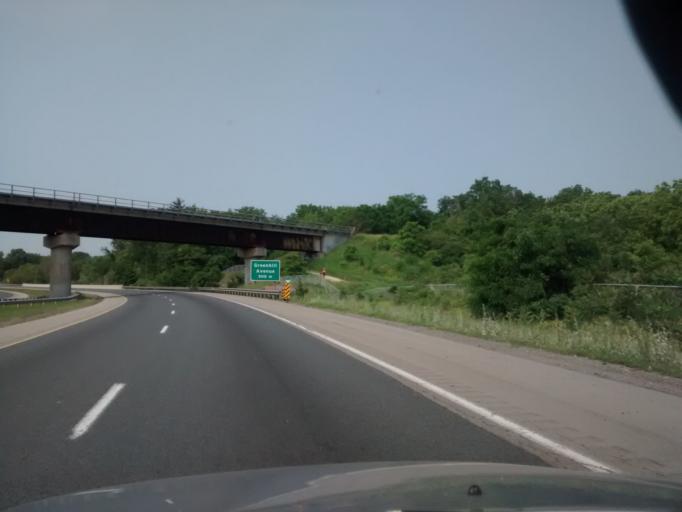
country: CA
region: Ontario
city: Hamilton
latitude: 43.2249
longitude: -79.7945
